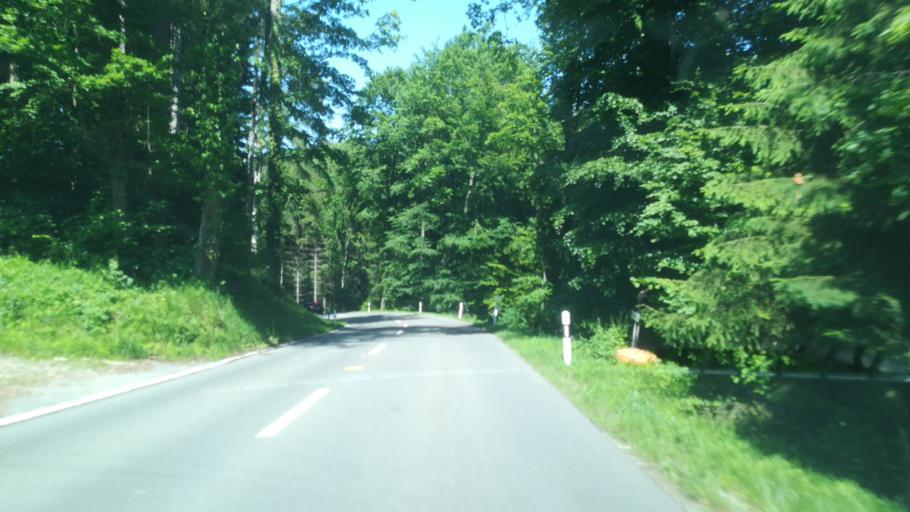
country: DE
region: Baden-Wuerttemberg
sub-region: Freiburg Region
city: Ohningen
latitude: 47.6359
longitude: 8.9215
